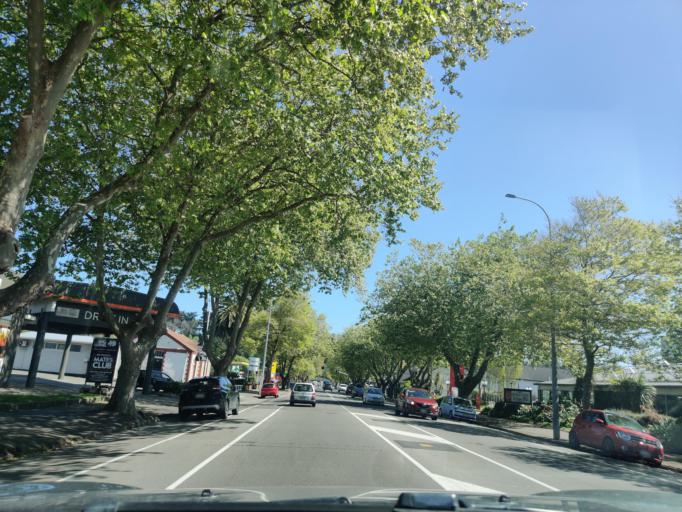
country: NZ
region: Manawatu-Wanganui
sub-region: Wanganui District
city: Wanganui
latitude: -39.9265
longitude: 175.0412
